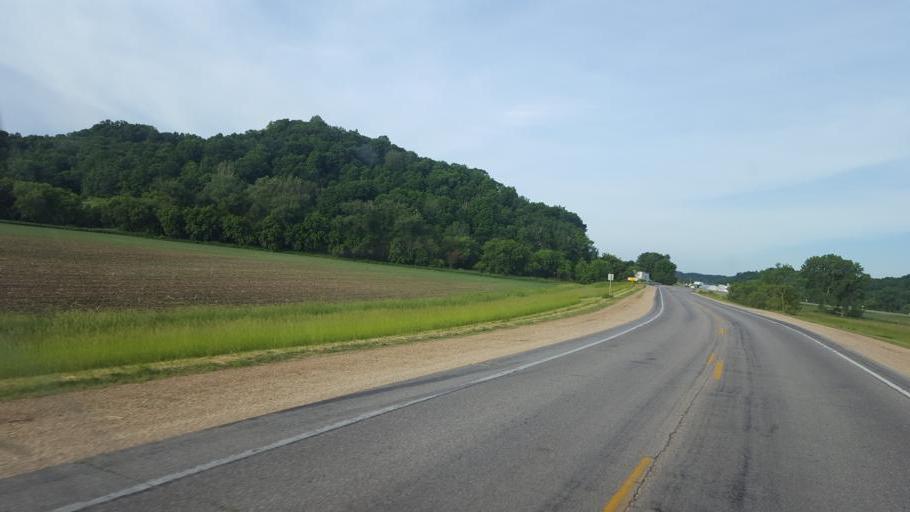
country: US
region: Wisconsin
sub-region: Vernon County
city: Hillsboro
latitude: 43.6591
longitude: -90.3858
